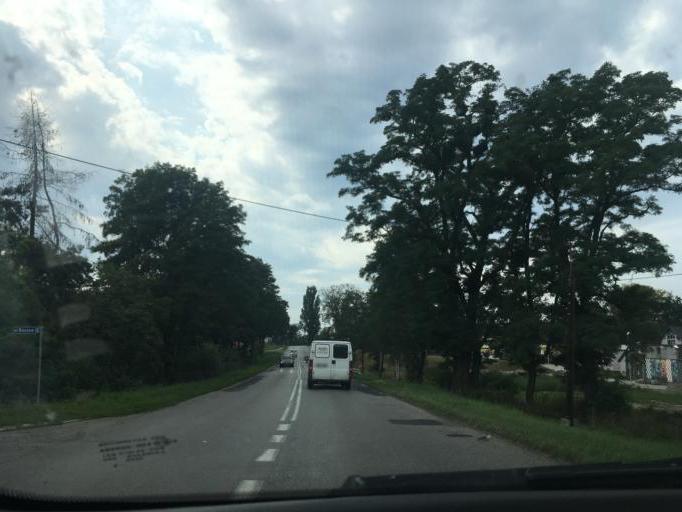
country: PL
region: Silesian Voivodeship
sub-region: Powiat raciborski
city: Kornowac
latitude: 50.0721
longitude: 18.3592
